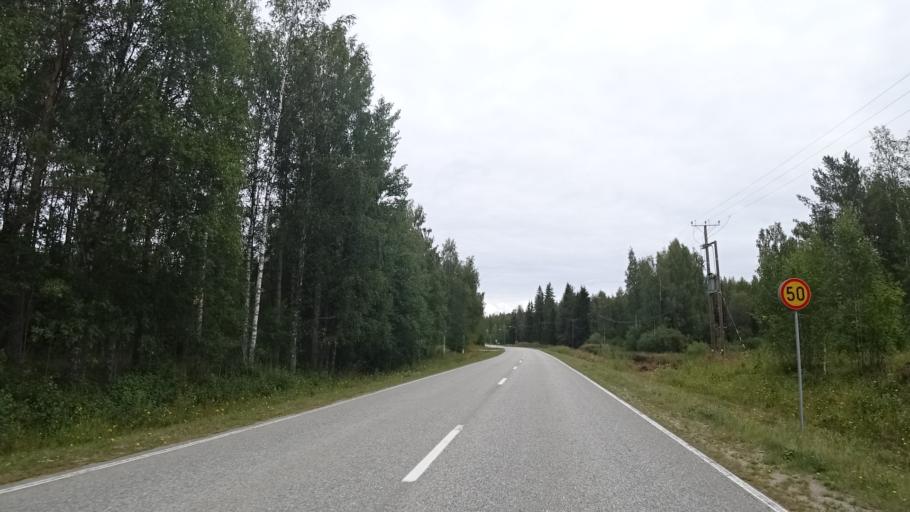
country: FI
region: North Karelia
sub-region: Joensuu
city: Ilomantsi
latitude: 62.6370
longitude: 31.2837
